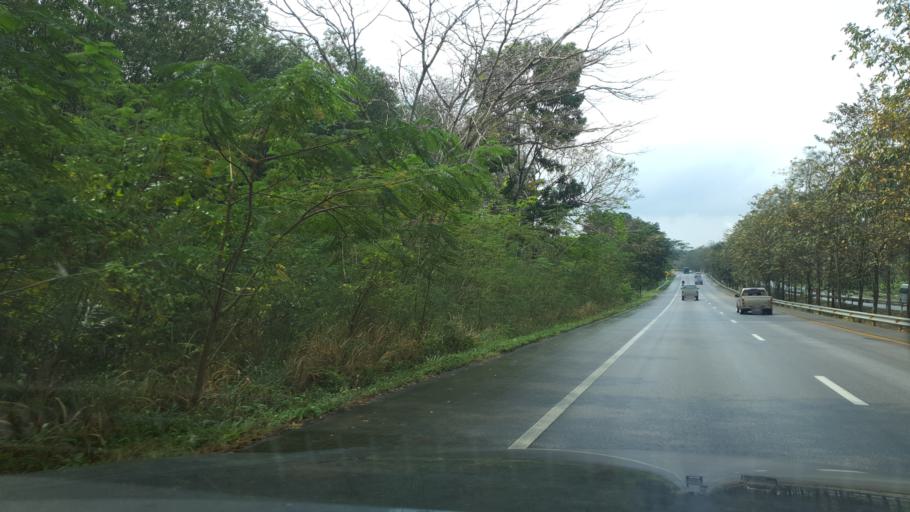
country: TH
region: Prachuap Khiri Khan
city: Bang Saphan Noi
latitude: 10.9484
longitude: 99.3010
